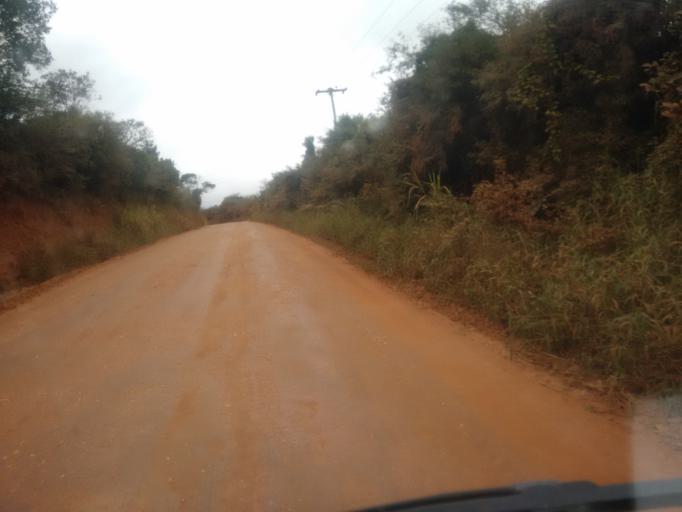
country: BR
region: Rio Grande do Sul
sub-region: Camaqua
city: Camaqua
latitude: -30.8200
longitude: -51.8140
